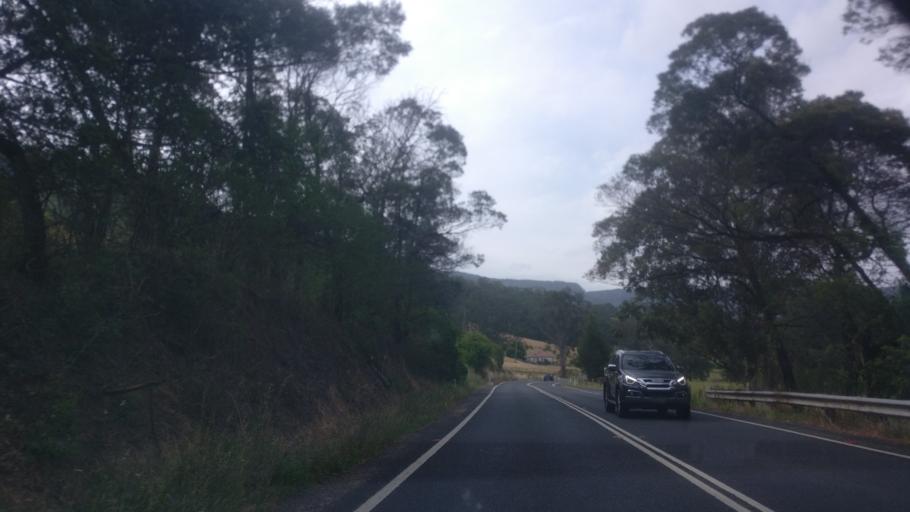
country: AU
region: New South Wales
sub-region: Shoalhaven Shire
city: Kangaroo Valley
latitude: -34.7098
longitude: 150.5284
